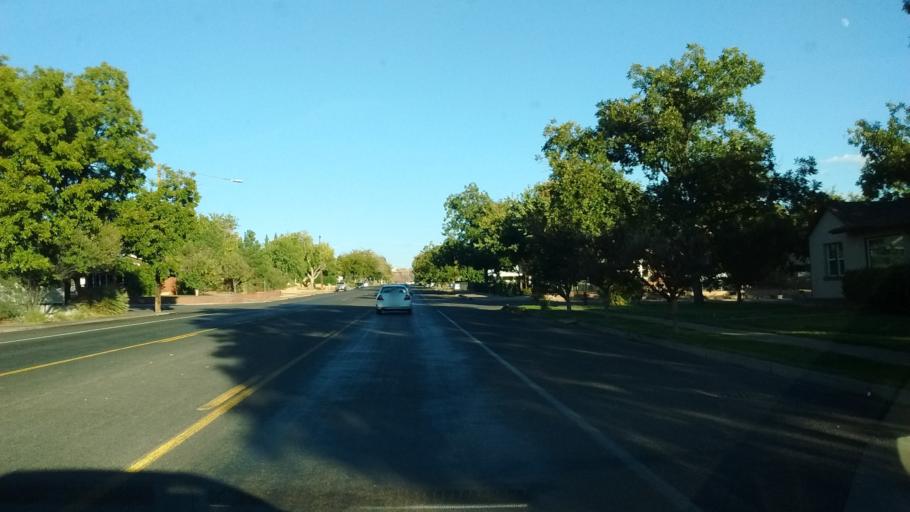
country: US
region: Utah
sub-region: Washington County
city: Saint George
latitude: 37.1065
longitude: -113.5734
